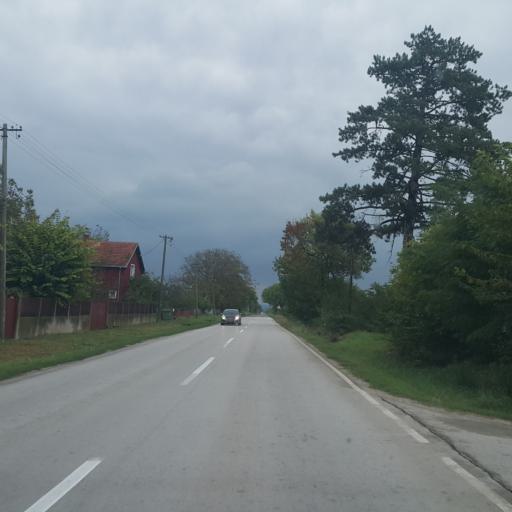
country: RS
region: Central Serbia
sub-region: Nisavski Okrug
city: Razanj
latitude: 43.6159
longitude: 21.5855
